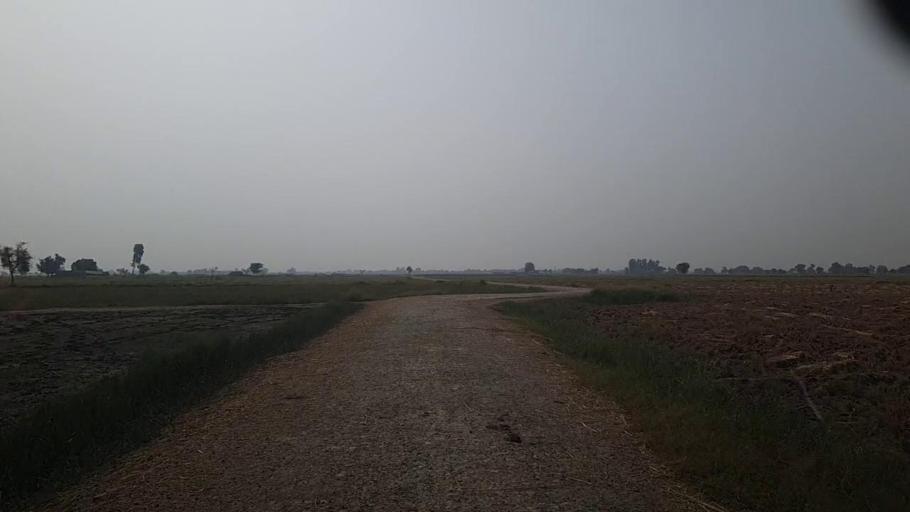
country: PK
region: Sindh
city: Kashmor
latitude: 28.3836
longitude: 69.4302
